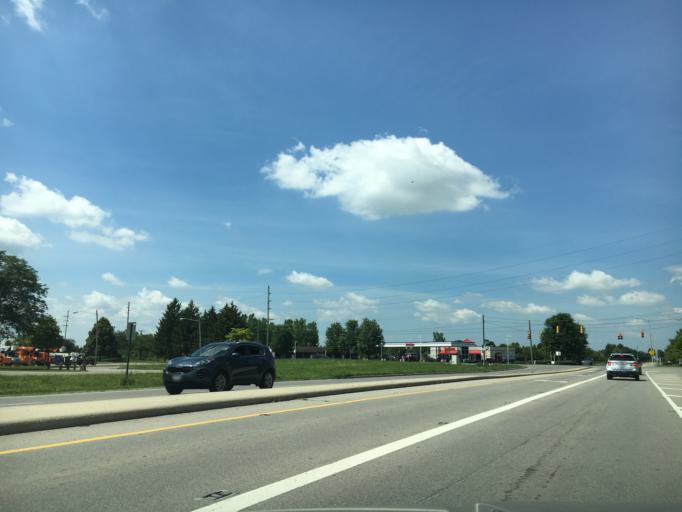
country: US
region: Ohio
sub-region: Franklin County
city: Lincoln Village
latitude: 39.9160
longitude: -83.1428
